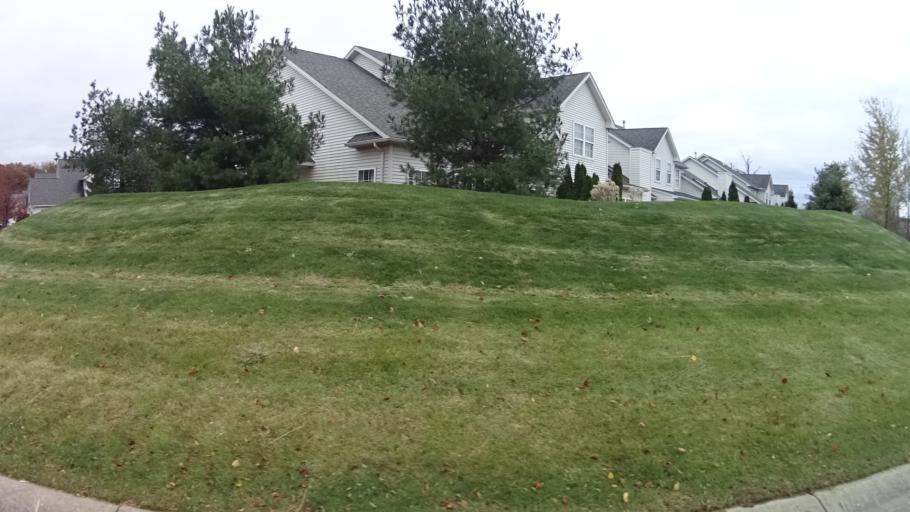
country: US
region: Ohio
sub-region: Lorain County
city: Avon Center
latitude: 41.4799
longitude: -82.0182
